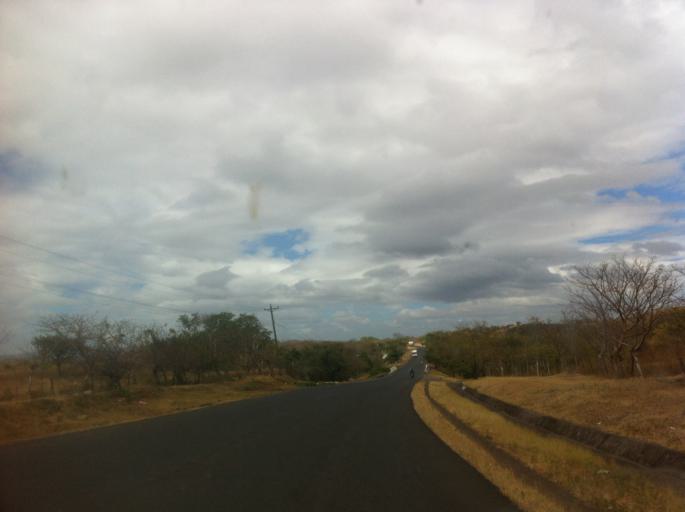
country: NI
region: Chontales
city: Juigalpa
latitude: 12.0835
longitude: -85.3349
